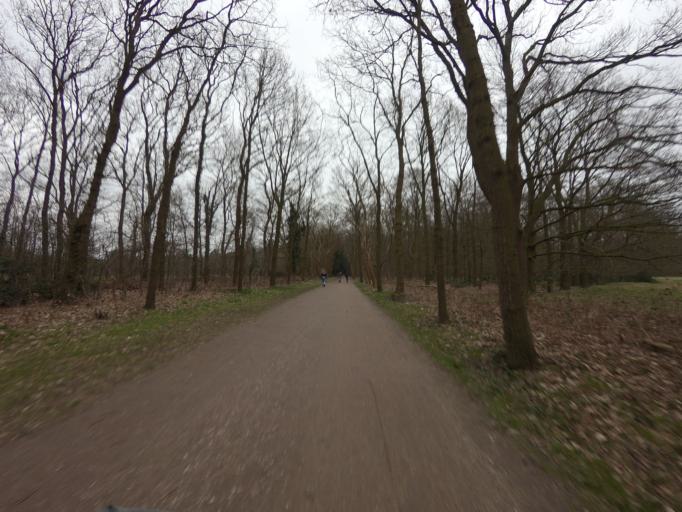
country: NL
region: North Holland
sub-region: Gemeente Hilversum
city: Hilversum
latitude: 52.2293
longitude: 5.1496
